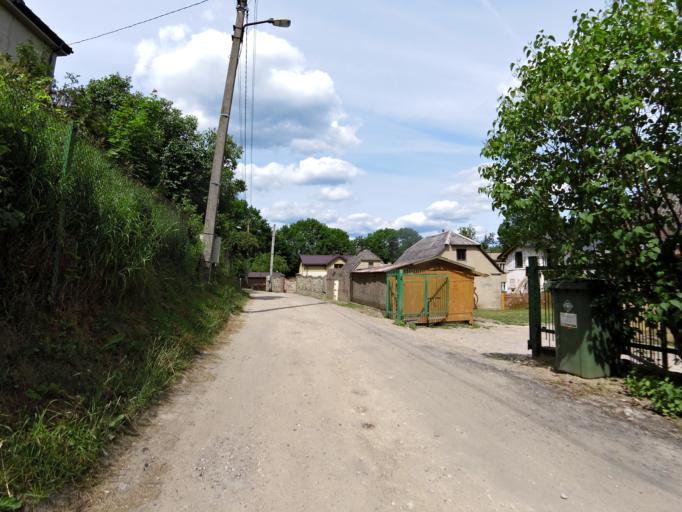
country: LT
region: Vilnius County
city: Rasos
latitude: 54.6706
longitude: 25.3180
